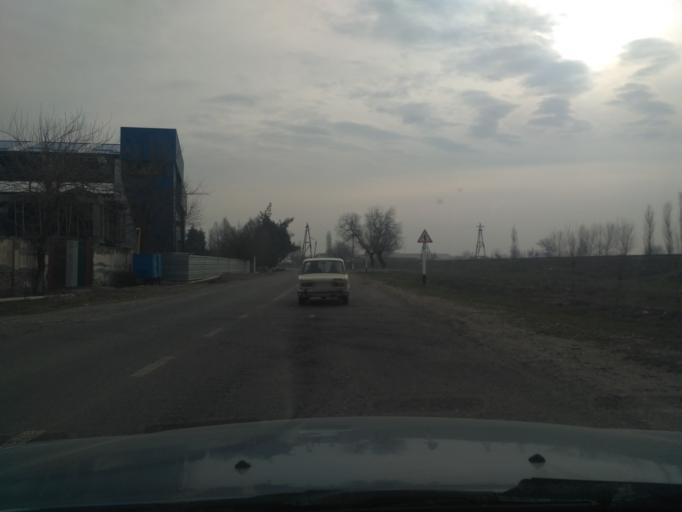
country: UZ
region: Sirdaryo
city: Sirdaryo
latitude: 40.8181
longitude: 68.6634
